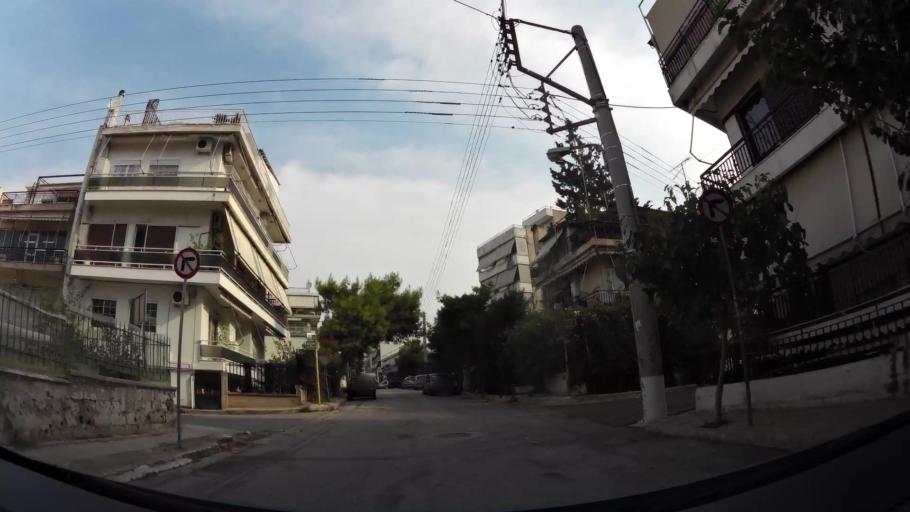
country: GR
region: Attica
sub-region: Nomarchia Athinas
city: Palaio Faliro
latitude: 37.9276
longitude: 23.7170
